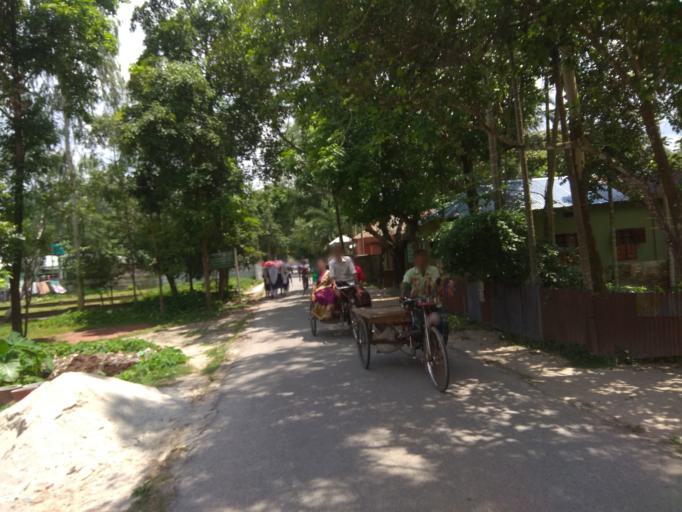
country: IN
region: West Bengal
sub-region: Koch Bihar
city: Haldibari
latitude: 26.1525
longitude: 88.9259
